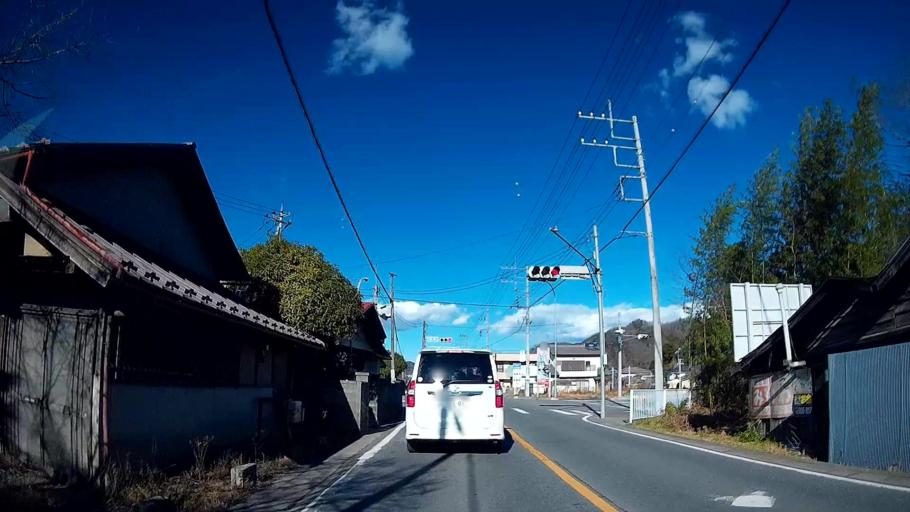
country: JP
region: Saitama
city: Yorii
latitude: 36.0860
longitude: 139.1127
